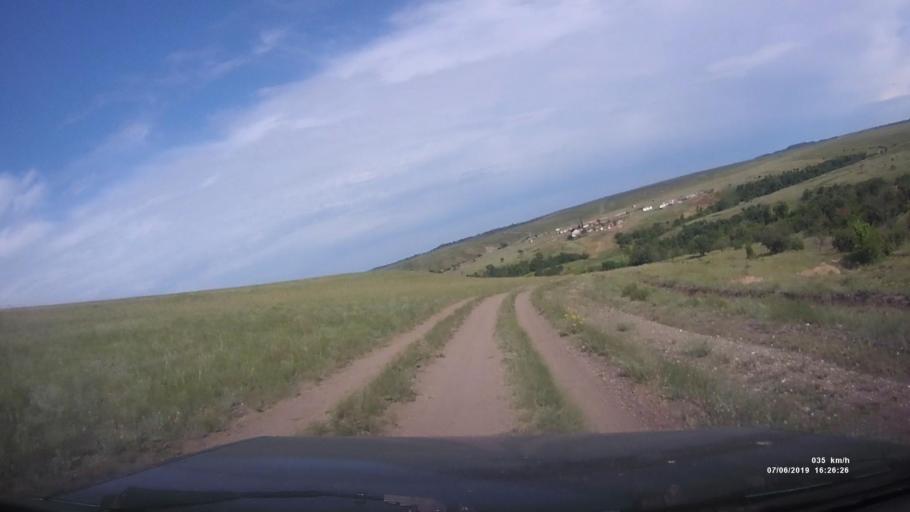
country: RU
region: Rostov
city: Kamensk-Shakhtinskiy
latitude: 48.2522
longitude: 40.3112
